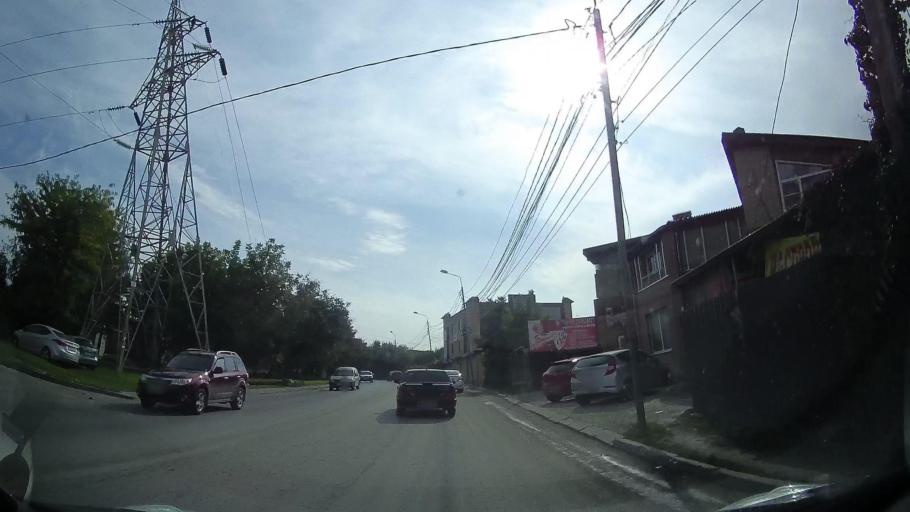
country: RU
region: Rostov
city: Severnyy
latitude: 47.2709
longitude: 39.7058
